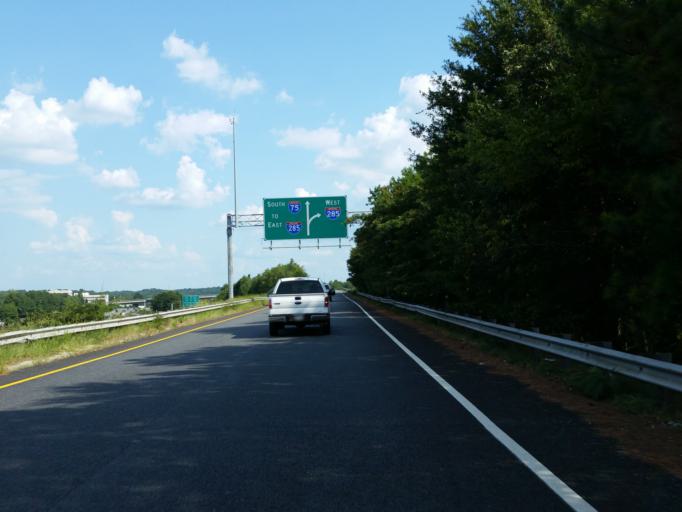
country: US
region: Georgia
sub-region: Cobb County
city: Vinings
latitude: 33.8992
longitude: -84.4718
